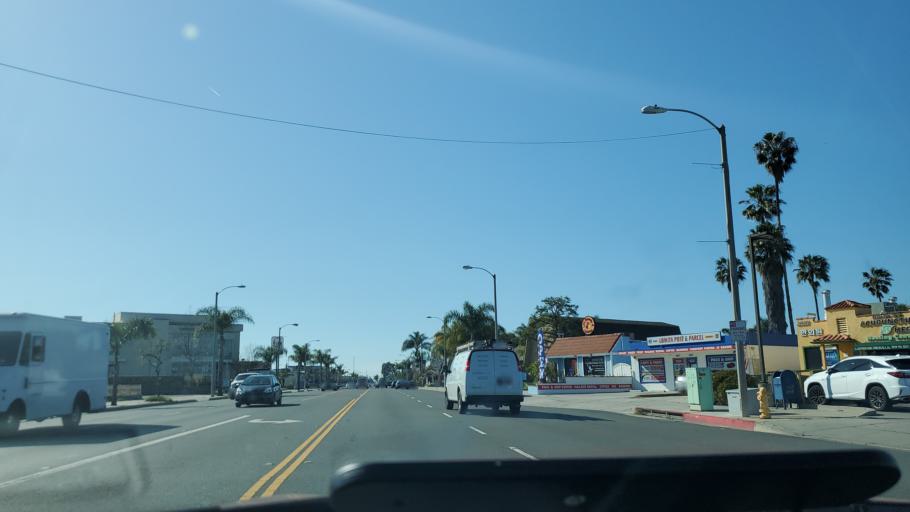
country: US
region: California
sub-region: Los Angeles County
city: Lomita
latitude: 33.8002
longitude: -118.3148
